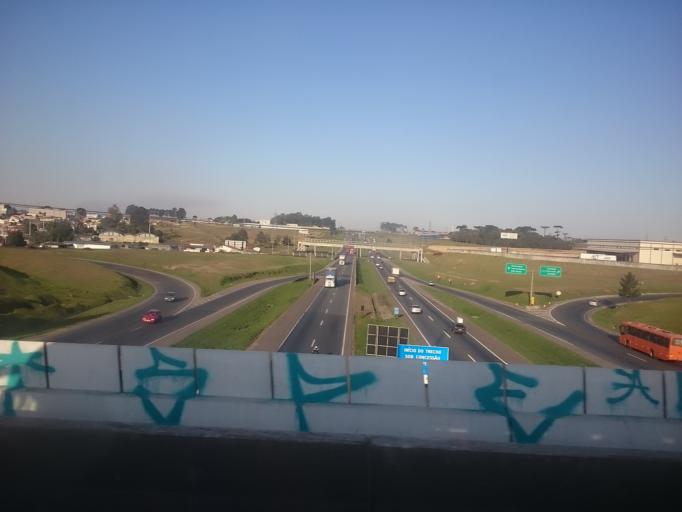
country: BR
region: Parana
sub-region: Sao Jose Dos Pinhais
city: Sao Jose dos Pinhais
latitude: -25.5444
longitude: -49.3032
